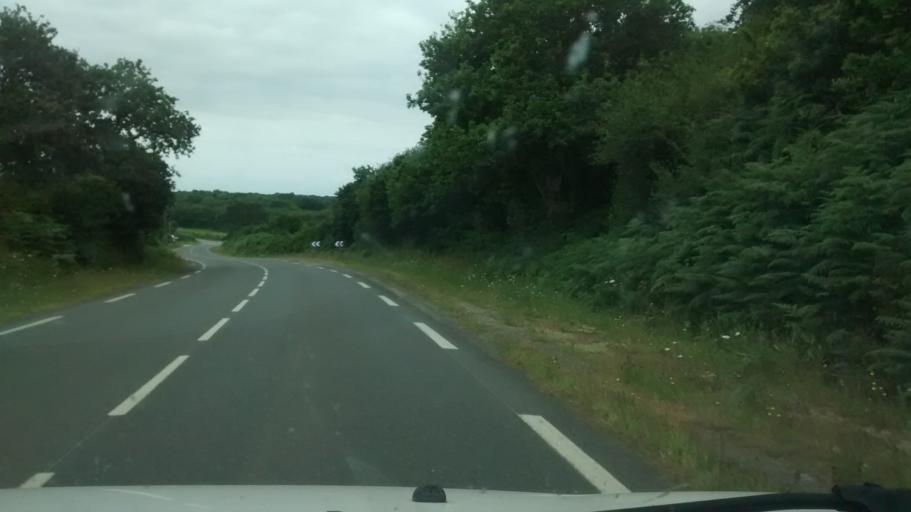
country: FR
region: Brittany
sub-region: Departement du Finistere
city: Plougastel-Daoulas
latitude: 48.3498
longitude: -4.4074
